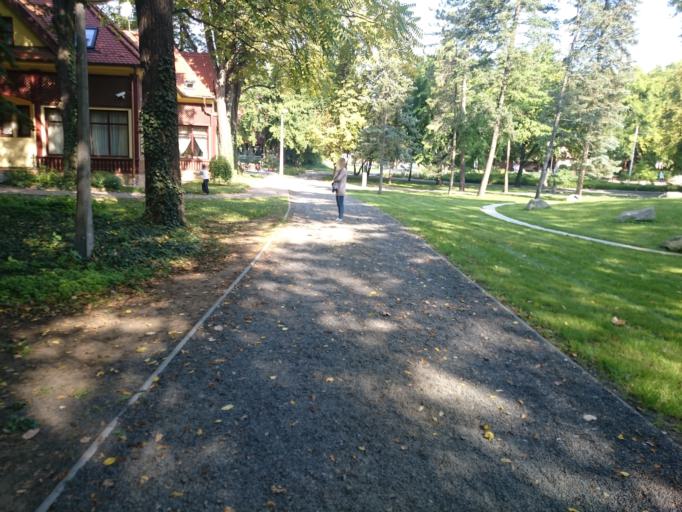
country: HU
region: Hajdu-Bihar
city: Debrecen
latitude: 47.5508
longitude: 21.6285
